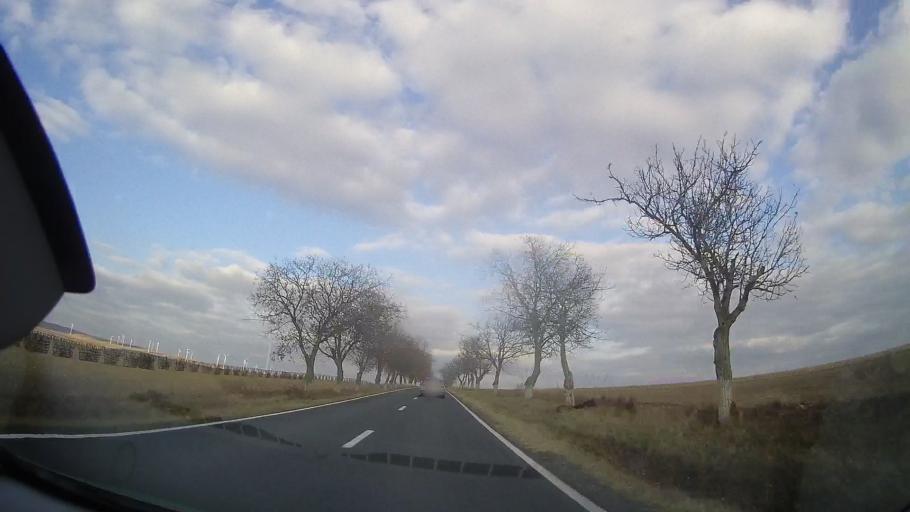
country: RO
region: Tulcea
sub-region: Comuna Topolog
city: Topolog
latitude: 44.8534
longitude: 28.3304
